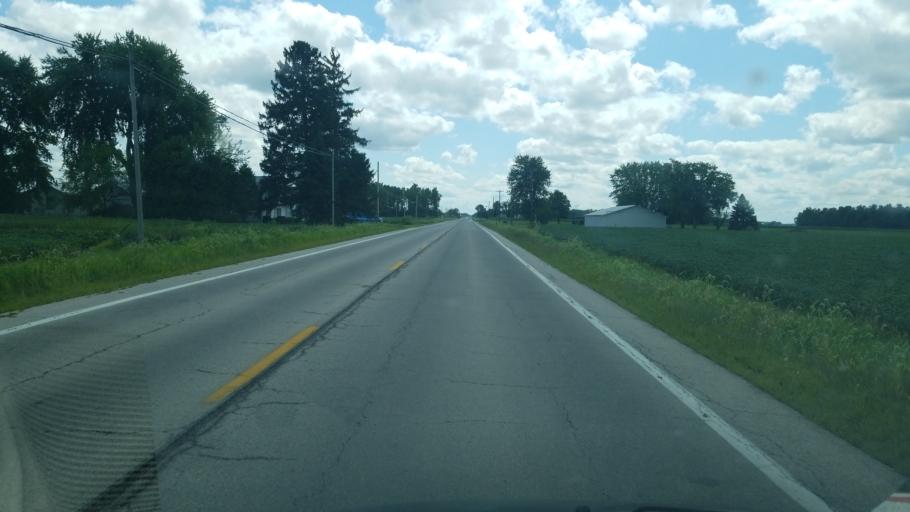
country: US
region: Ohio
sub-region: Henry County
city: Napoleon
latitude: 41.3458
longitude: -84.1195
